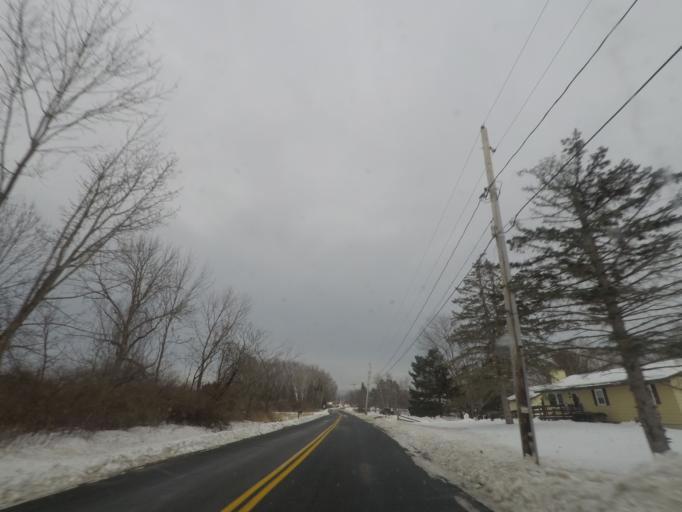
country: US
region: New York
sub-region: Rensselaer County
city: Castleton-on-Hudson
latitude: 42.5124
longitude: -73.7133
